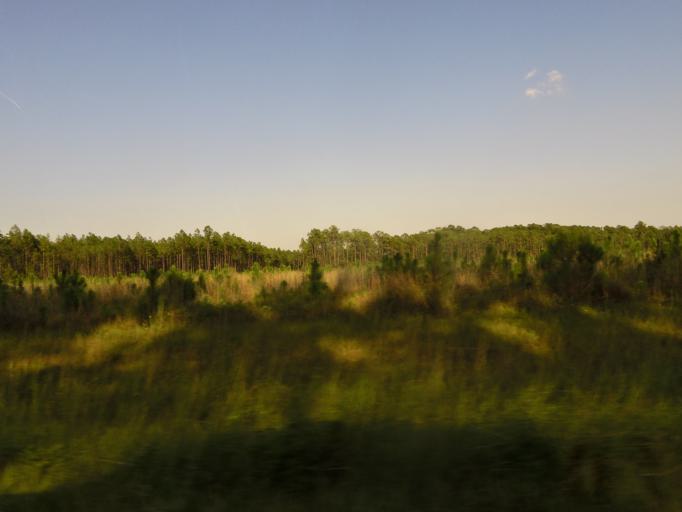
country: US
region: Florida
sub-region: Duval County
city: Baldwin
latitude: 30.3431
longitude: -82.0091
